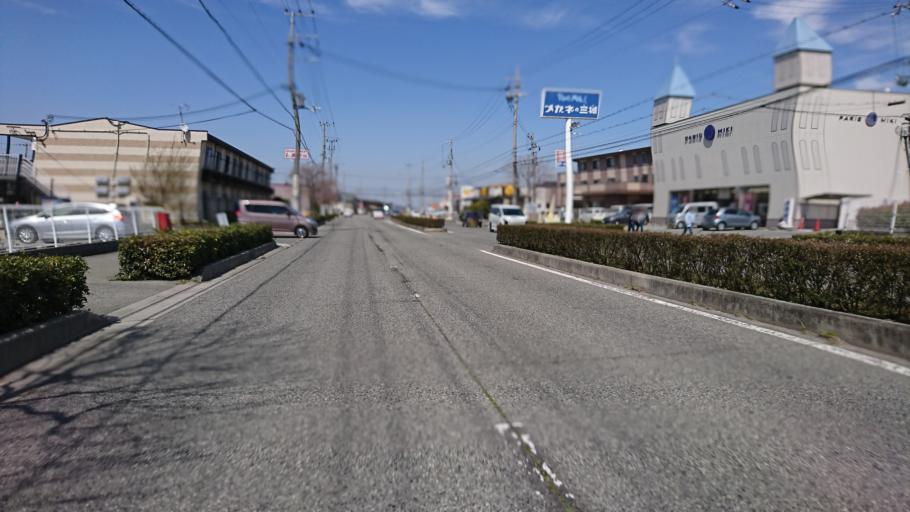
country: JP
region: Hyogo
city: Miki
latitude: 34.7486
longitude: 134.9157
